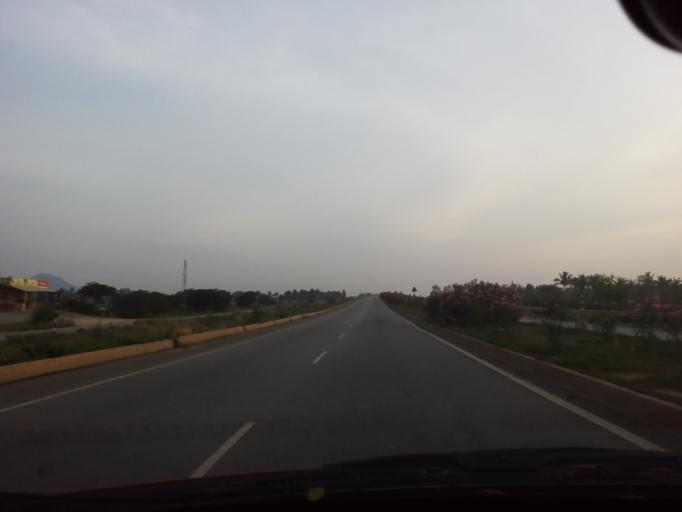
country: IN
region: Karnataka
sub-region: Chikkaballapur
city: Chik Ballapur
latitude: 13.3463
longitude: 77.7255
